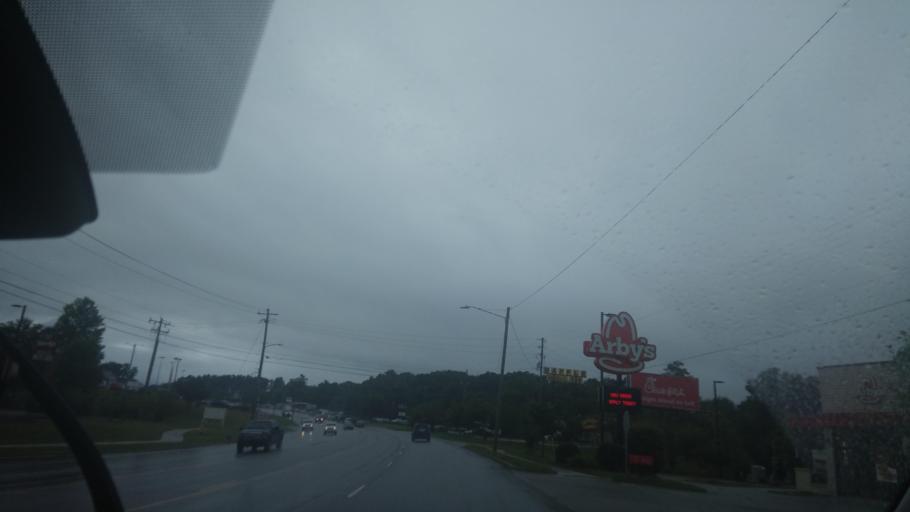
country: US
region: North Carolina
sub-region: Buncombe County
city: Bent Creek
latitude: 35.5608
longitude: -82.6337
